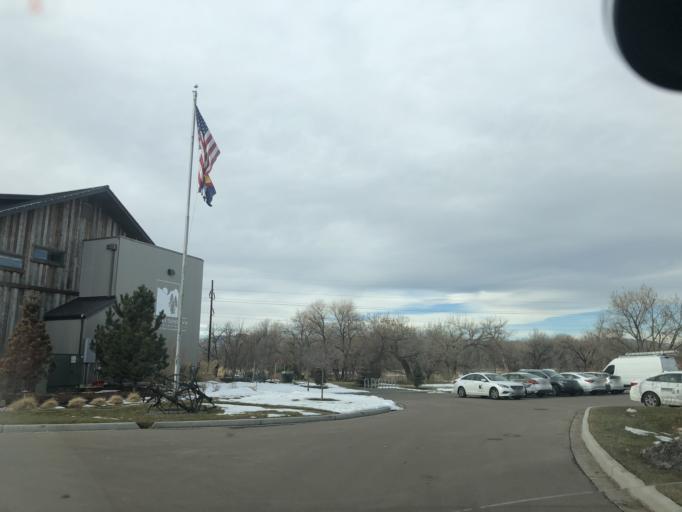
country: US
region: Colorado
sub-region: Arapahoe County
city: Columbine Valley
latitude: 39.5927
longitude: -105.0249
